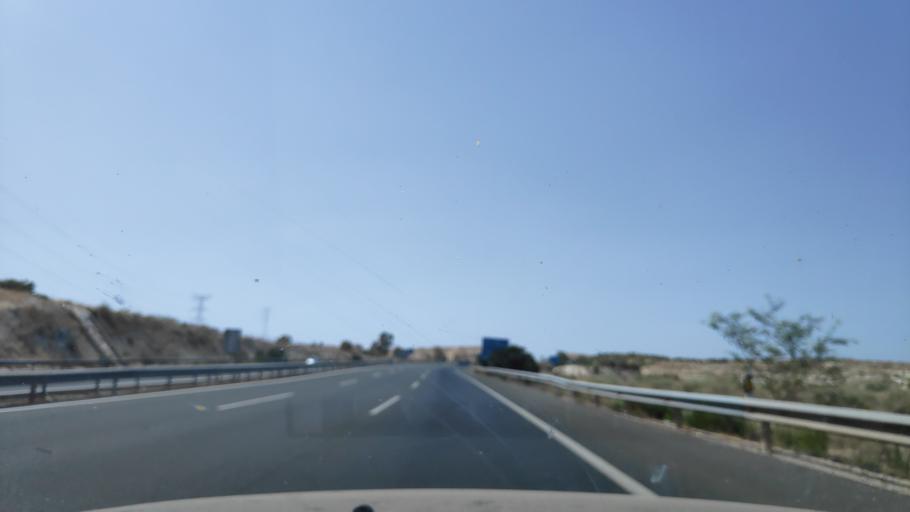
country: ES
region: Murcia
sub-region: Murcia
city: Murcia
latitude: 37.8748
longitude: -1.1278
